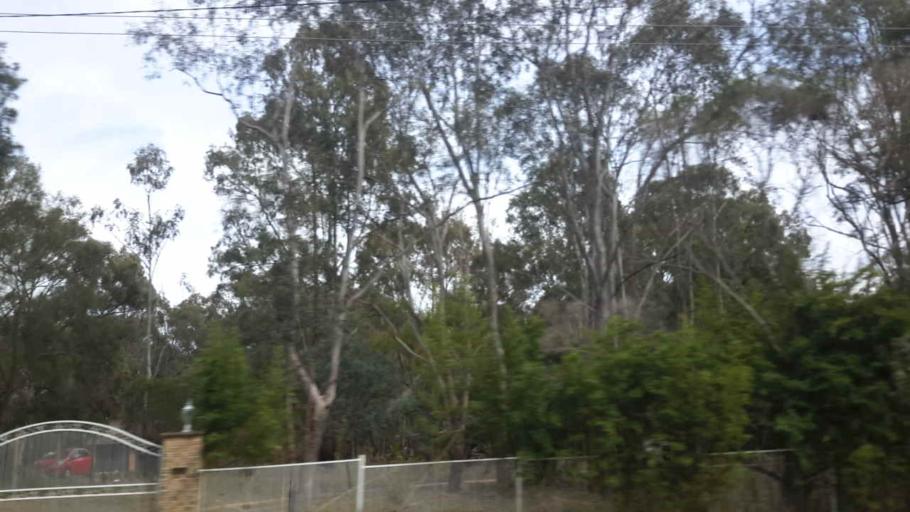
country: AU
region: New South Wales
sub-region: Hawkesbury
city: South Windsor
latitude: -33.6474
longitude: 150.7795
